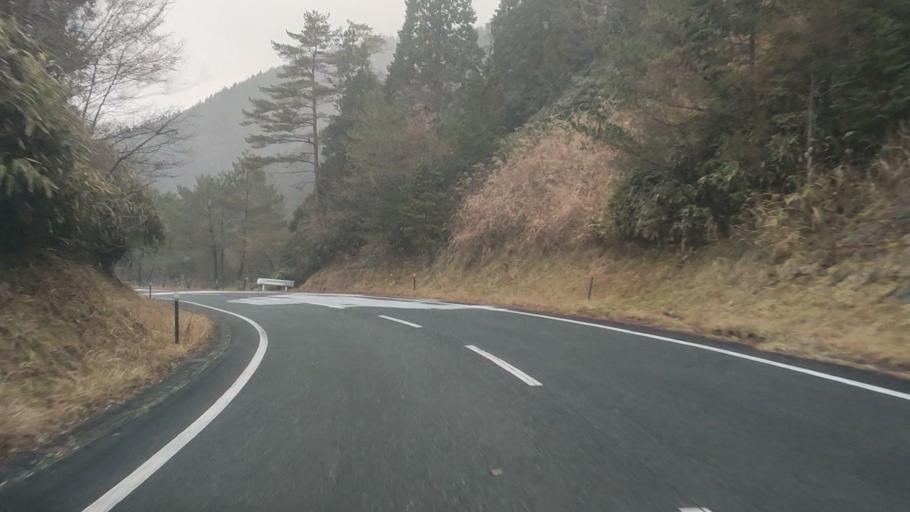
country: JP
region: Kumamoto
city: Matsubase
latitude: 32.5672
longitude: 130.9095
